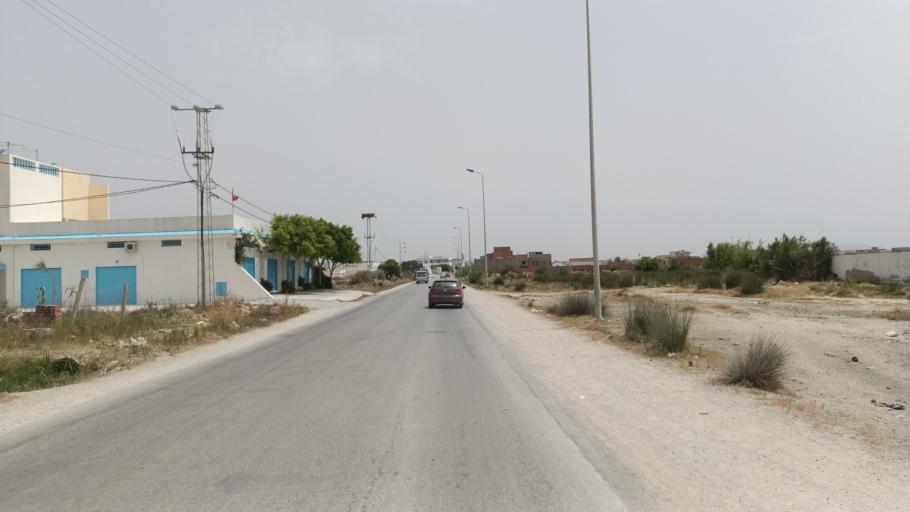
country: TN
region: Nabul
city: Manzil Bu Zalafah
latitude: 36.7103
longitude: 10.4827
